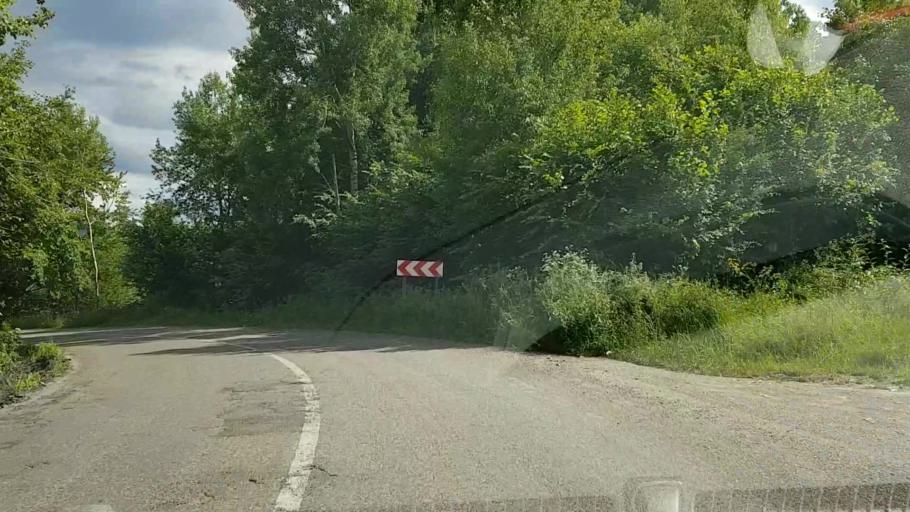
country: RO
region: Neamt
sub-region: Comuna Ceahlau
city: Ceahlau
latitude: 47.0636
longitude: 25.9628
